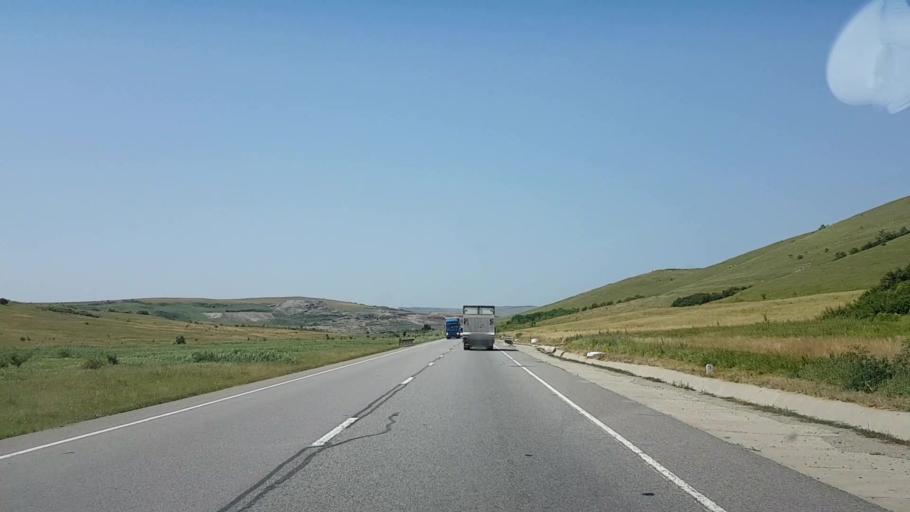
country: RO
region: Cluj
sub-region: Comuna Apahida
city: Dezmir
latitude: 46.7533
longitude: 23.7022
